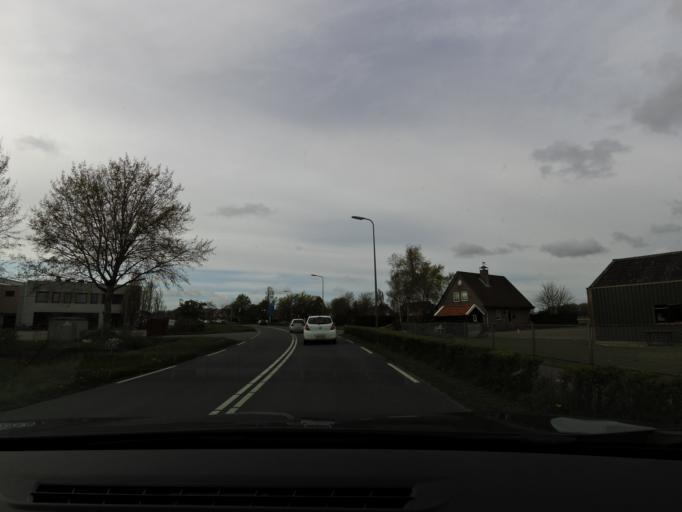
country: NL
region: South Holland
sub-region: Gemeente Lisse
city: Lisse
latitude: 52.2900
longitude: 4.5289
